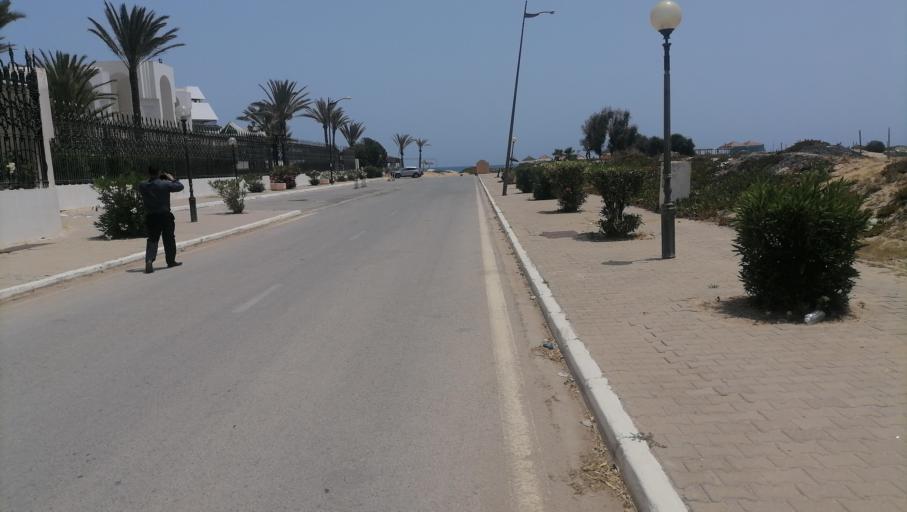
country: TN
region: Nabul
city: Al Hammamat
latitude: 36.3543
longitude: 10.5282
